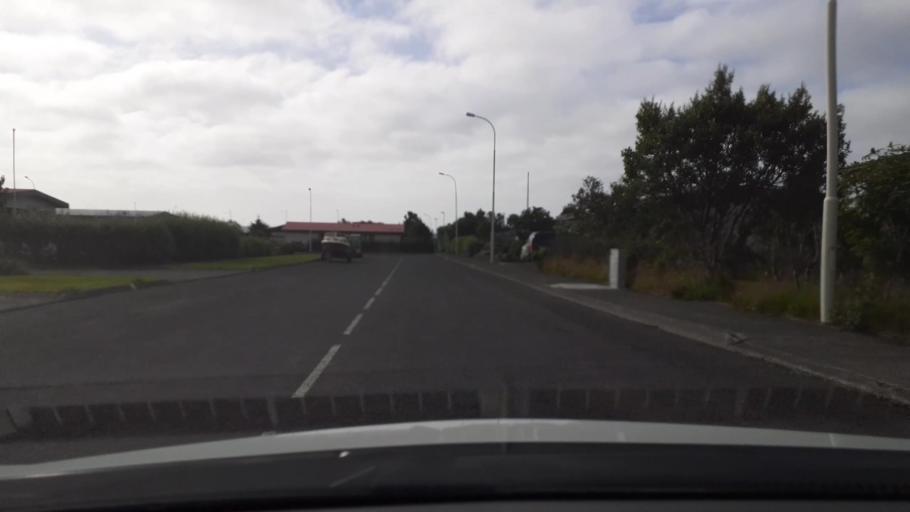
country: IS
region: South
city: THorlakshoefn
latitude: 63.8543
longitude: -21.3930
